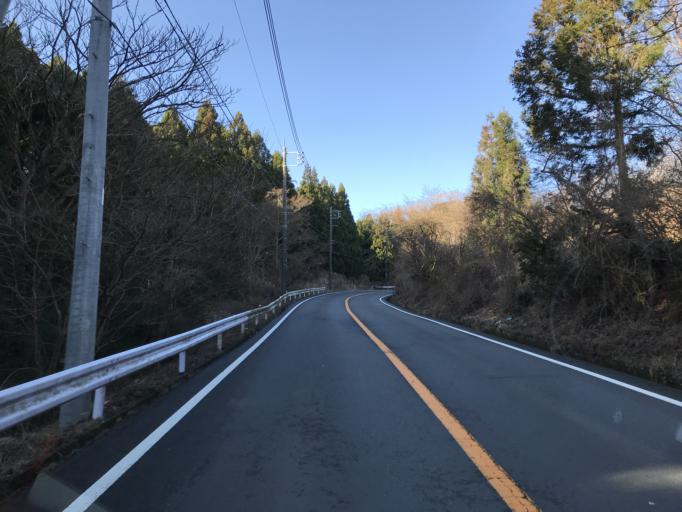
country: JP
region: Shizuoka
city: Gotemba
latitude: 35.2609
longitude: 138.8345
